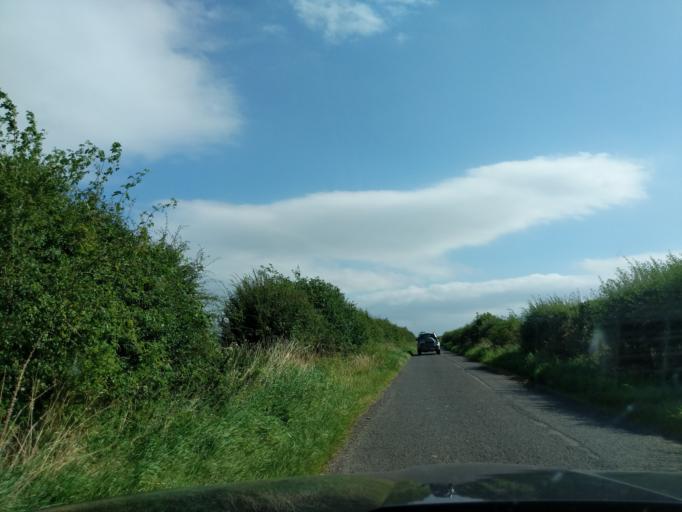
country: GB
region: England
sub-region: Northumberland
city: Ford
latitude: 55.6663
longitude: -2.1635
